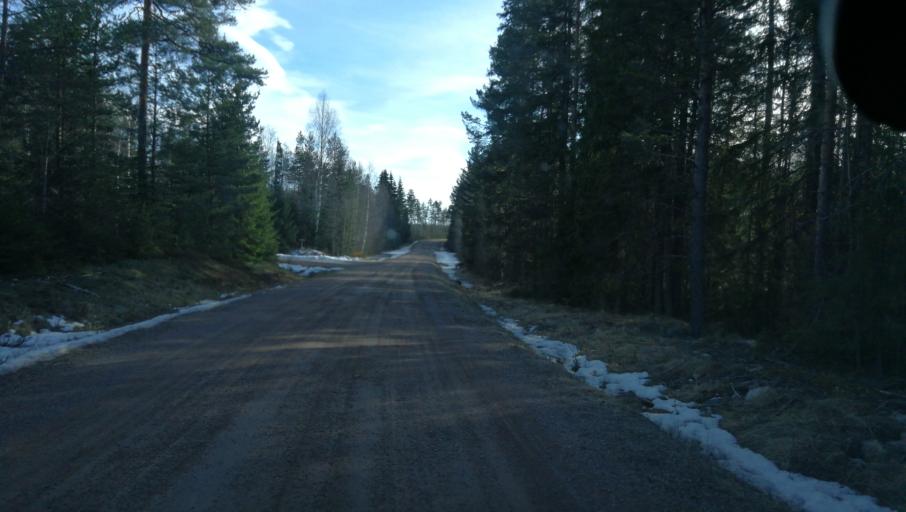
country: SE
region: Dalarna
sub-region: Vansbro Kommun
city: Vansbro
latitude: 60.8229
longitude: 14.1942
